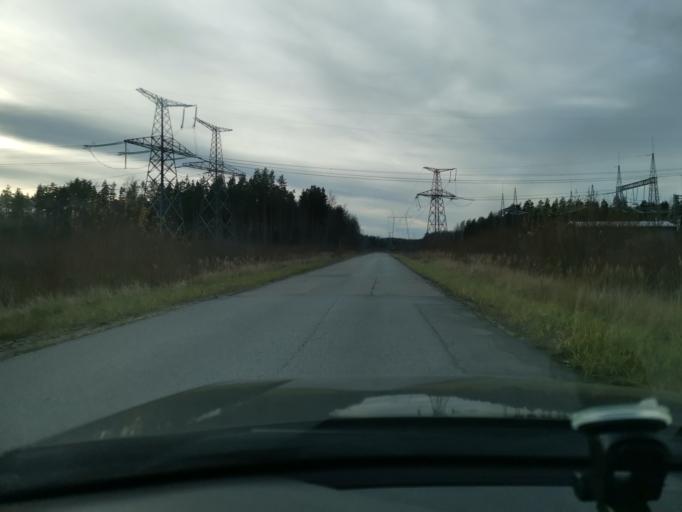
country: EE
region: Ida-Virumaa
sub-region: Sillamaee linn
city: Sillamae
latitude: 59.2674
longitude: 27.9053
